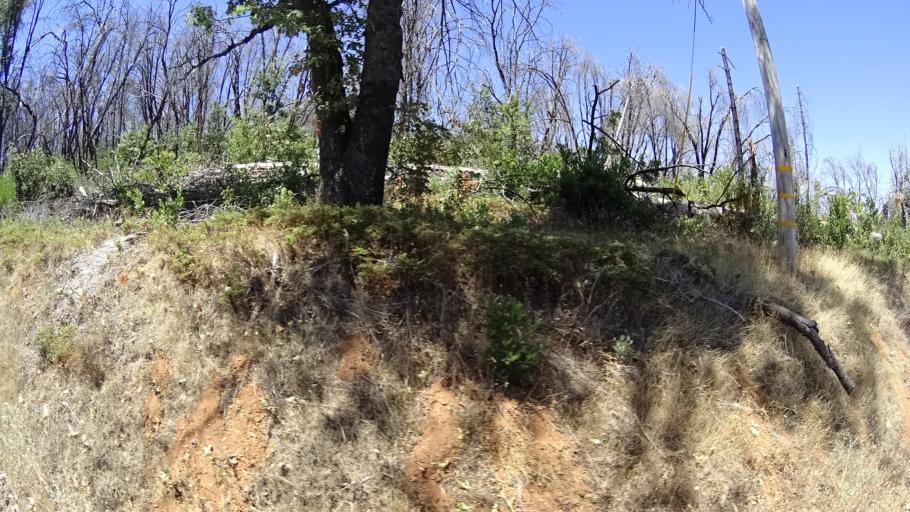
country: US
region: California
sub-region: Calaveras County
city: Mountain Ranch
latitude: 38.2308
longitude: -120.5882
